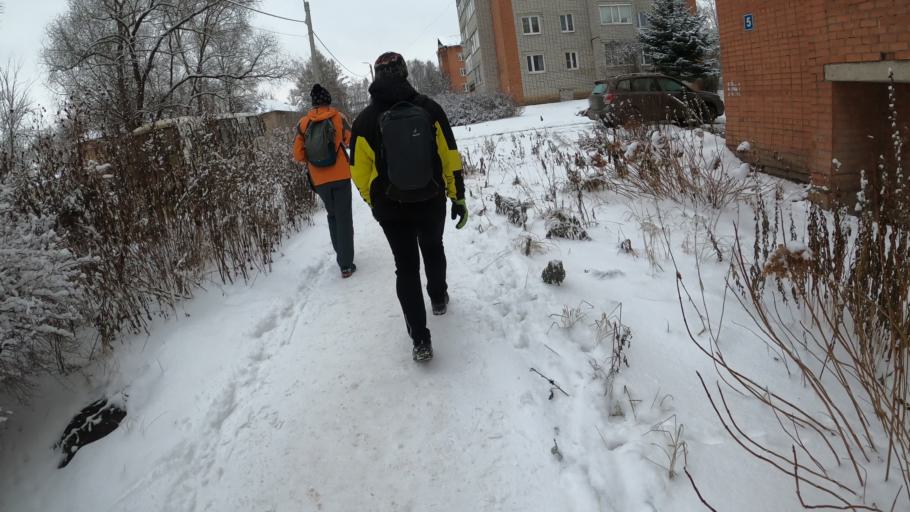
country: RU
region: Jaroslavl
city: Pereslavl'-Zalesskiy
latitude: 56.7396
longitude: 38.8866
